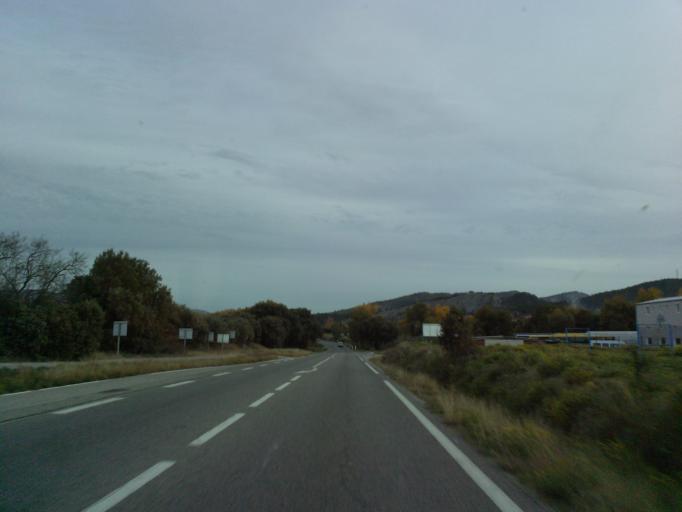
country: FR
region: Provence-Alpes-Cote d'Azur
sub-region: Departement des Alpes-de-Haute-Provence
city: Peipin
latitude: 44.1362
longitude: 5.9700
